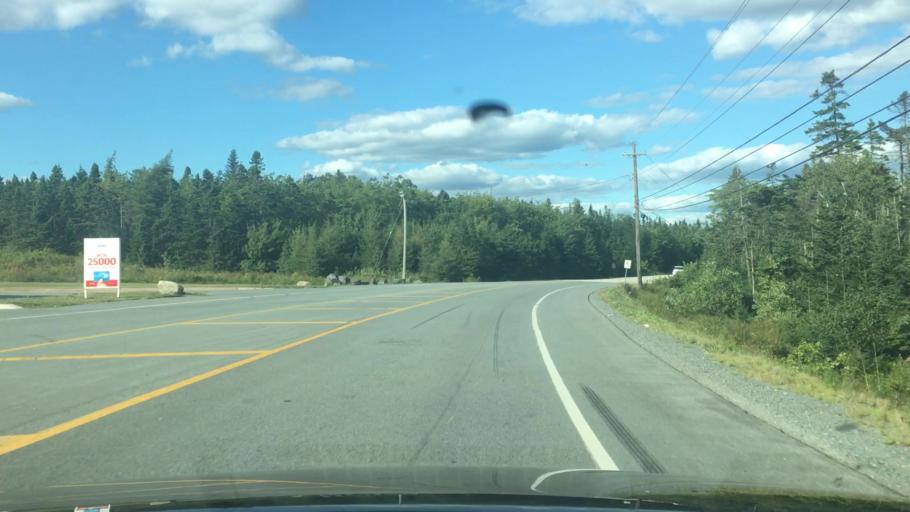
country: CA
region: Nova Scotia
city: Halifax
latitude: 44.6078
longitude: -63.6725
